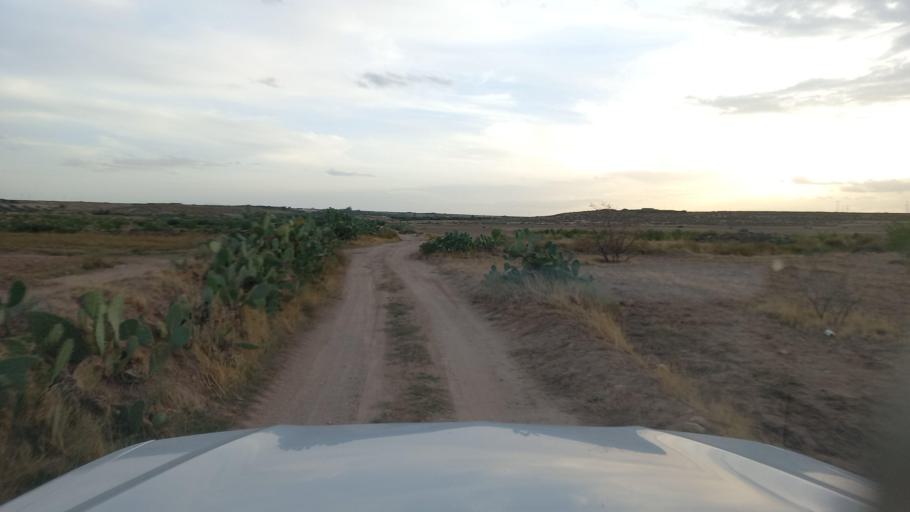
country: TN
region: Al Qasrayn
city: Sbiba
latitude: 35.4145
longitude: 9.0852
